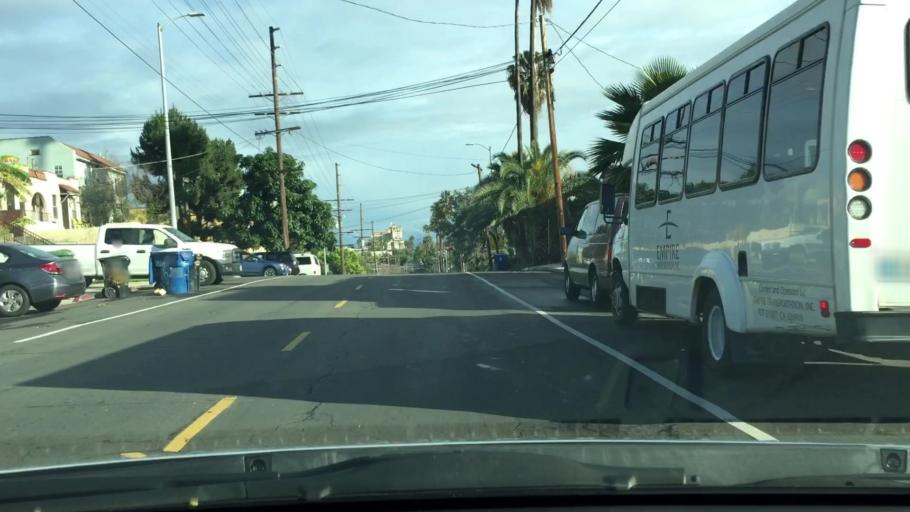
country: US
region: California
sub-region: Los Angeles County
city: Silver Lake
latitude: 34.0801
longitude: -118.2832
